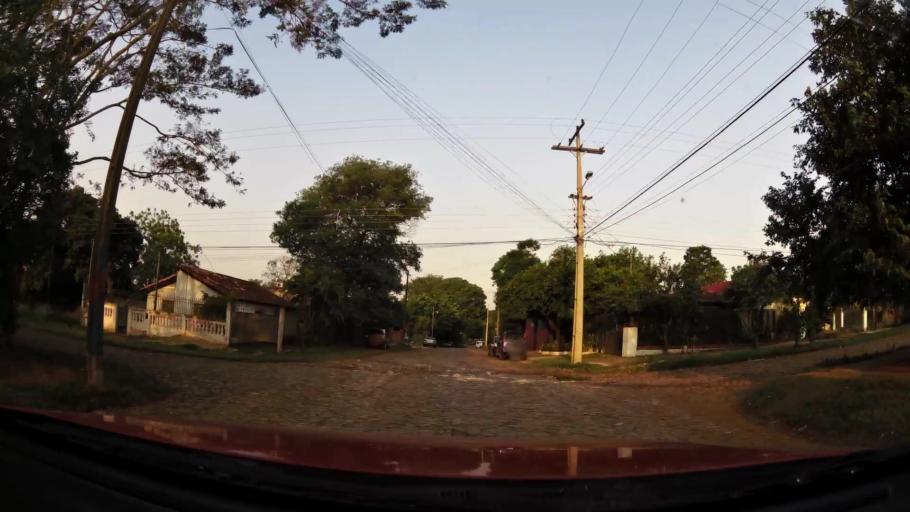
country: PY
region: Central
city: Lambare
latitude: -25.3523
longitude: -57.6024
